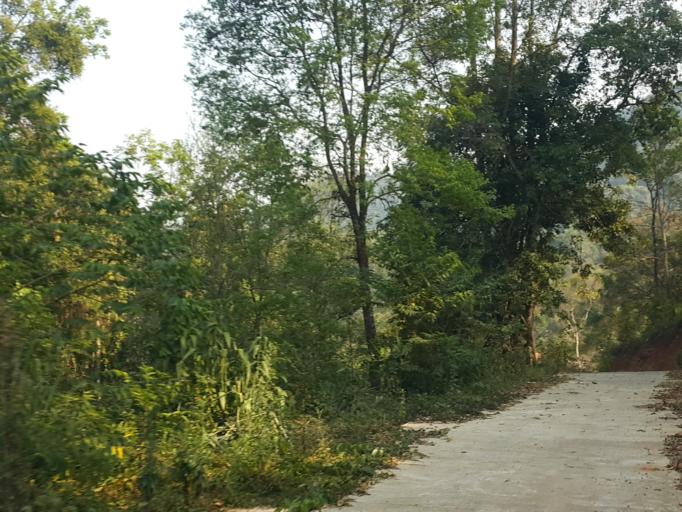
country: TH
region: Chiang Mai
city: Samoeng
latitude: 19.0204
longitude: 98.7631
